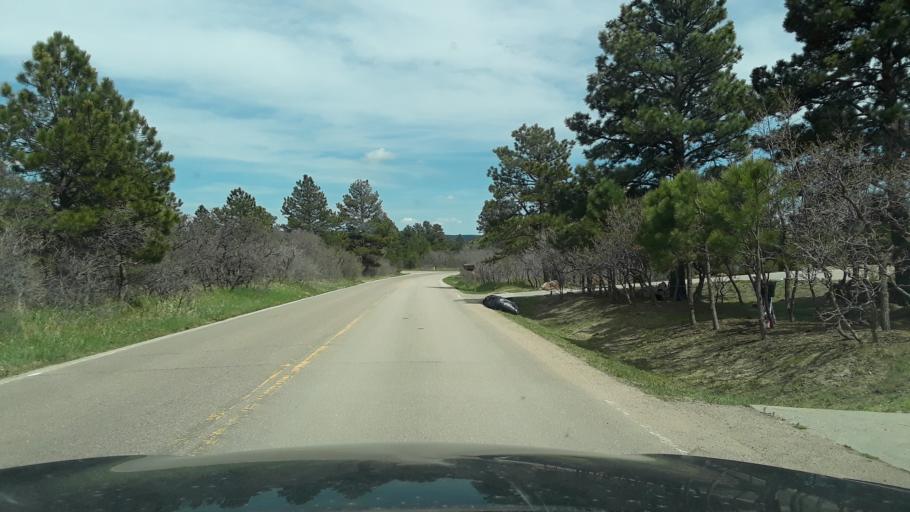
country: US
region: Colorado
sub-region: El Paso County
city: Monument
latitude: 39.0896
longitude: -104.8953
